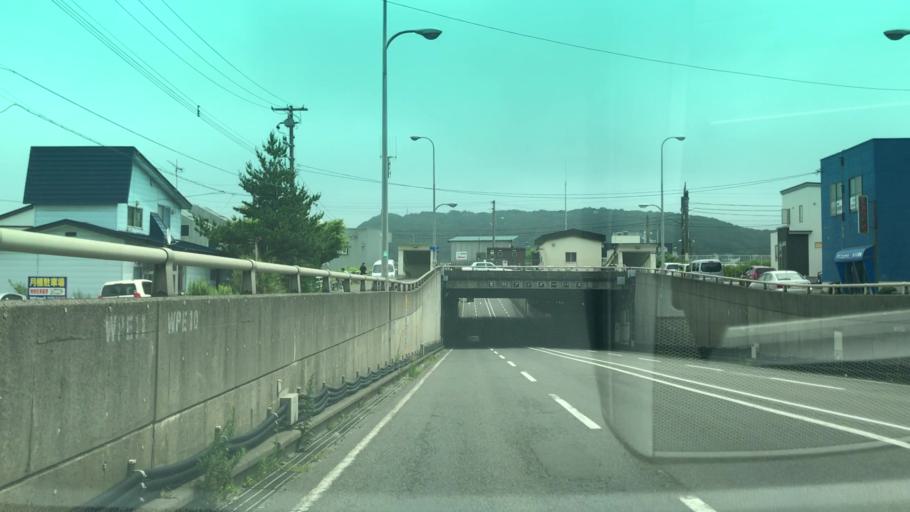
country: JP
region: Hokkaido
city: Muroran
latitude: 42.3603
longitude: 141.0421
